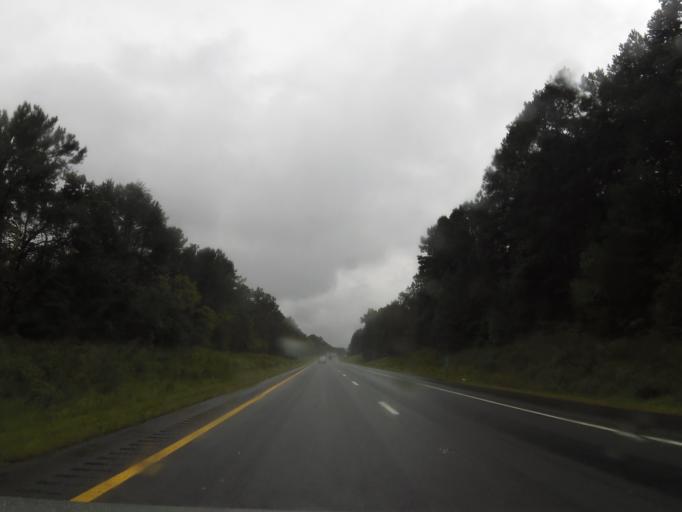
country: US
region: Tennessee
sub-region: Bradley County
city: Hopewell
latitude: 35.2543
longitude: -84.8379
